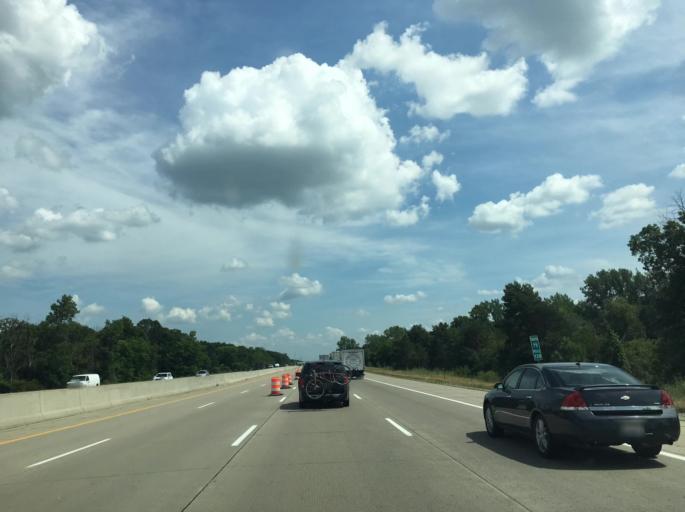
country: US
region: Michigan
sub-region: Saginaw County
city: Birch Run
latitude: 43.2783
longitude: -83.8043
